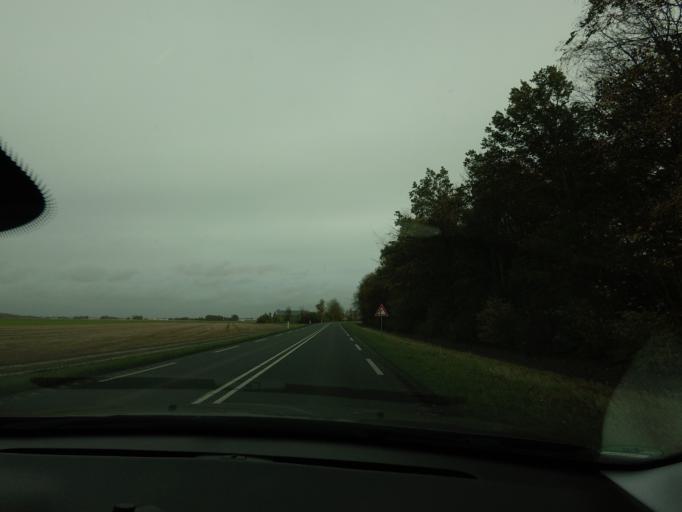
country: NL
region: Flevoland
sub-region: Gemeente Noordoostpolder
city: Ens
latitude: 52.7129
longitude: 5.8558
